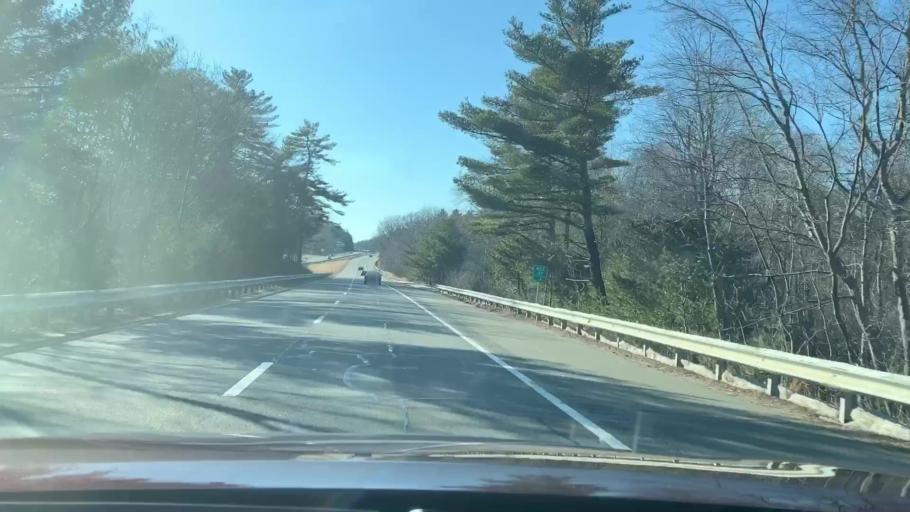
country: US
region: Massachusetts
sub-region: Essex County
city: Essex
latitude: 42.5914
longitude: -70.7848
